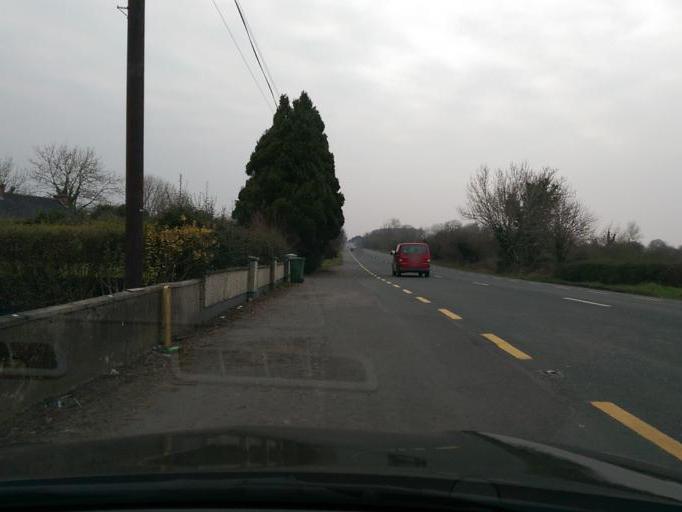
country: IE
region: Leinster
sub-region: An Iarmhi
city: Athlone
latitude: 53.4351
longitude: -7.9688
